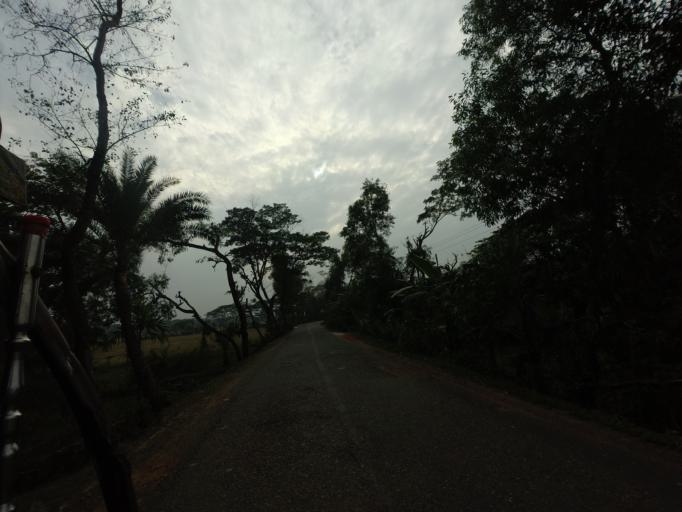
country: BD
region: Barisal
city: Nalchiti
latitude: 22.4554
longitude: 90.3497
